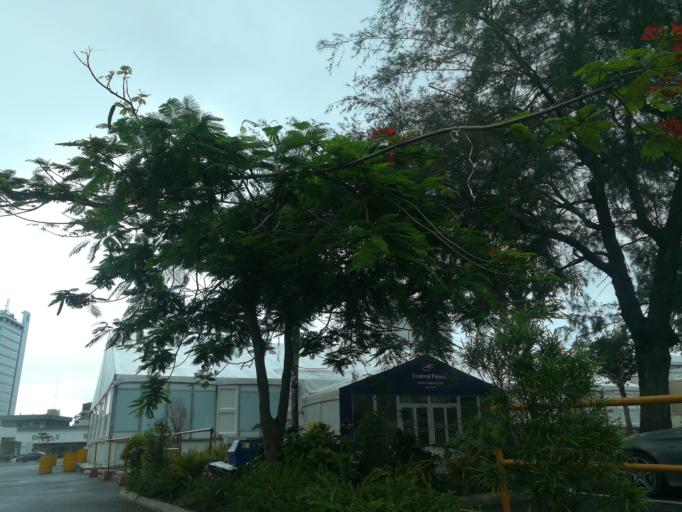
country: NG
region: Lagos
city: Lagos
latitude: 6.4305
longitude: 3.4078
